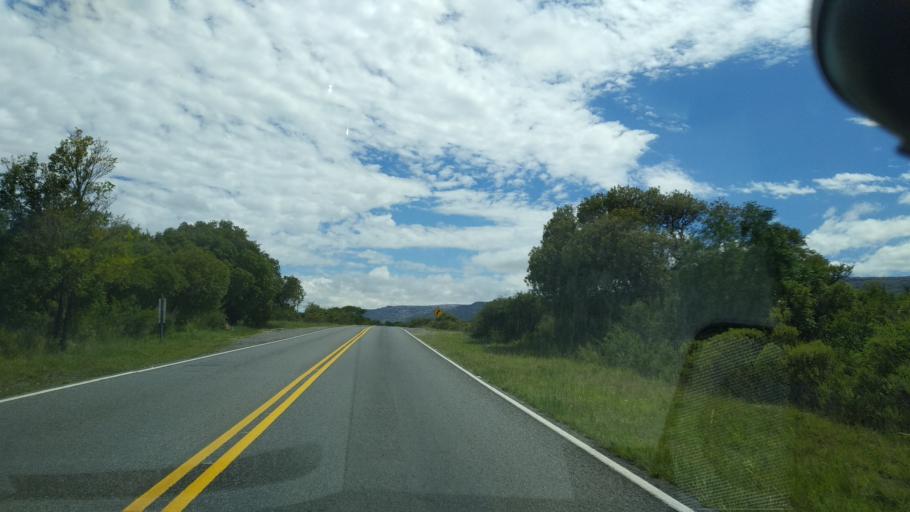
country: AR
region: Cordoba
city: Mina Clavero
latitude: -31.7524
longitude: -64.9518
